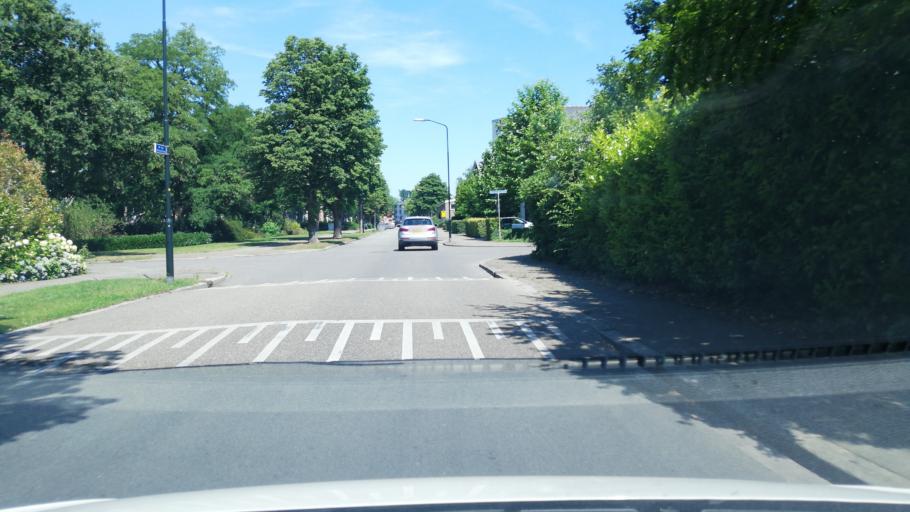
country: NL
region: Gelderland
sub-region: Gemeente Apeldoorn
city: Apeldoorn
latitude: 52.2270
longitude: 5.9606
